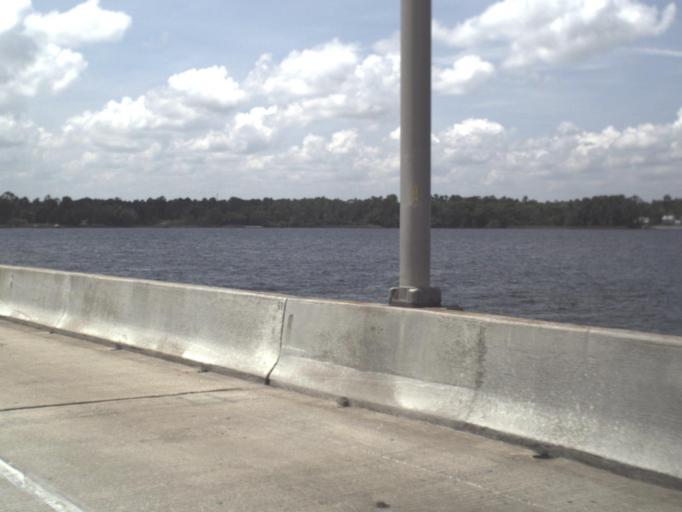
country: US
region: Florida
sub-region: Clay County
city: Orange Park
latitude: 30.1909
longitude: -81.6806
